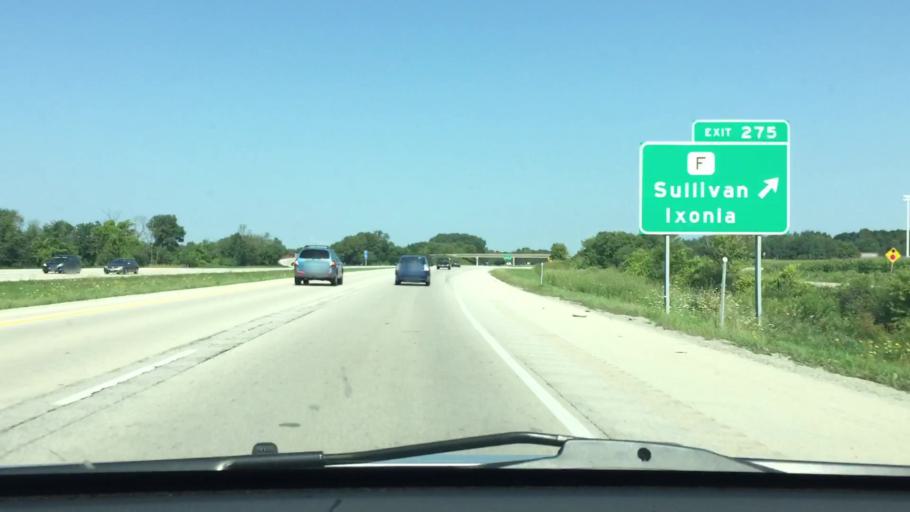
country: US
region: Wisconsin
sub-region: Jefferson County
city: Ixonia
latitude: 43.0724
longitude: -88.5869
